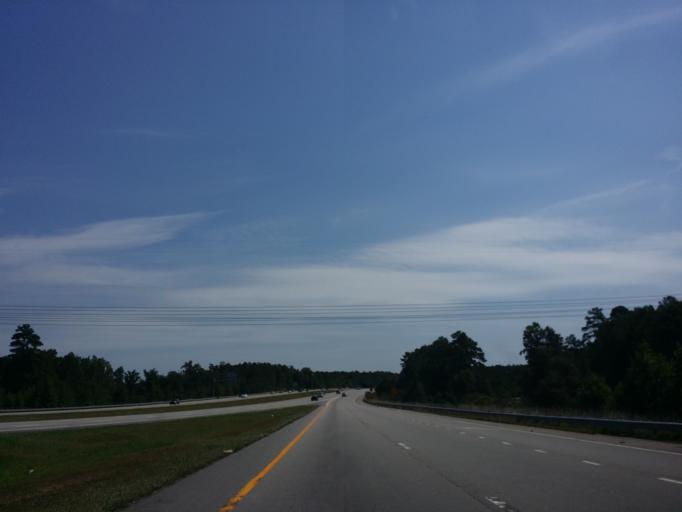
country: US
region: North Carolina
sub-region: Wake County
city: Morrisville
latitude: 35.9075
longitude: -78.7648
